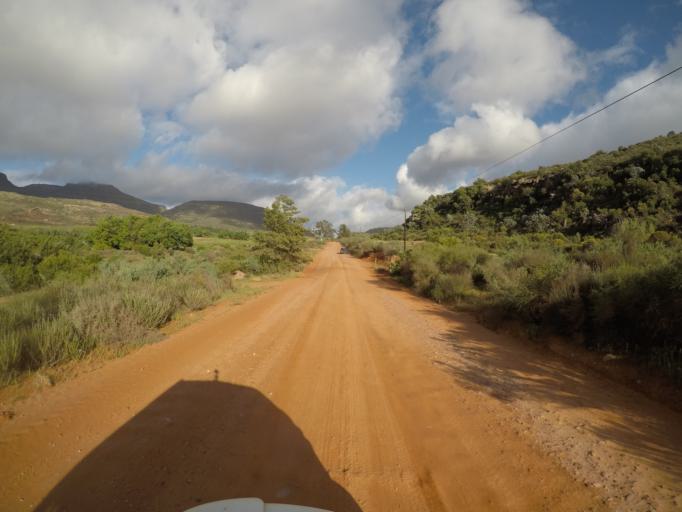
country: ZA
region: Western Cape
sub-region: West Coast District Municipality
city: Clanwilliam
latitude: -32.3432
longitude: 18.8132
